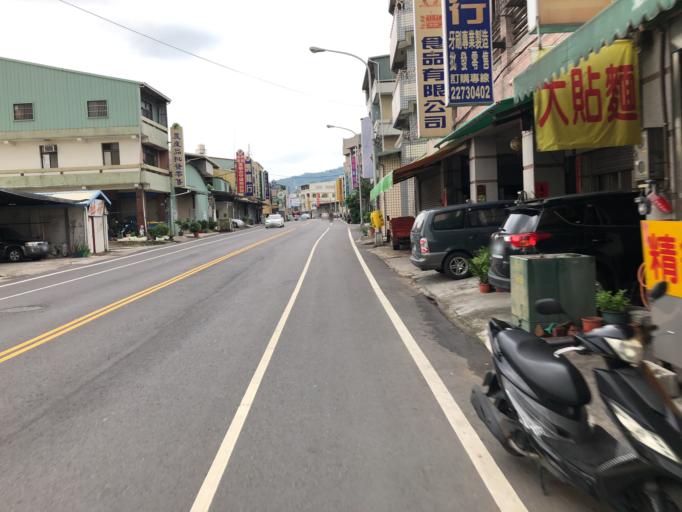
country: TW
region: Taiwan
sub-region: Taichung City
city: Taichung
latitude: 24.1126
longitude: 120.7312
